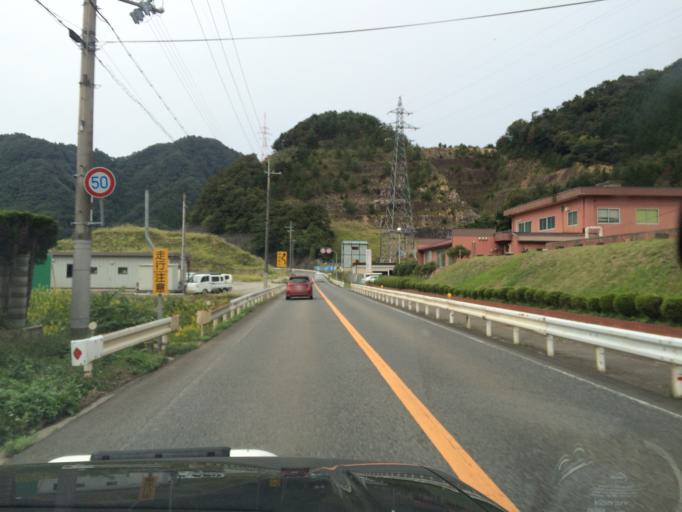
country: JP
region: Hyogo
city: Toyooka
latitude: 35.4043
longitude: 134.7833
